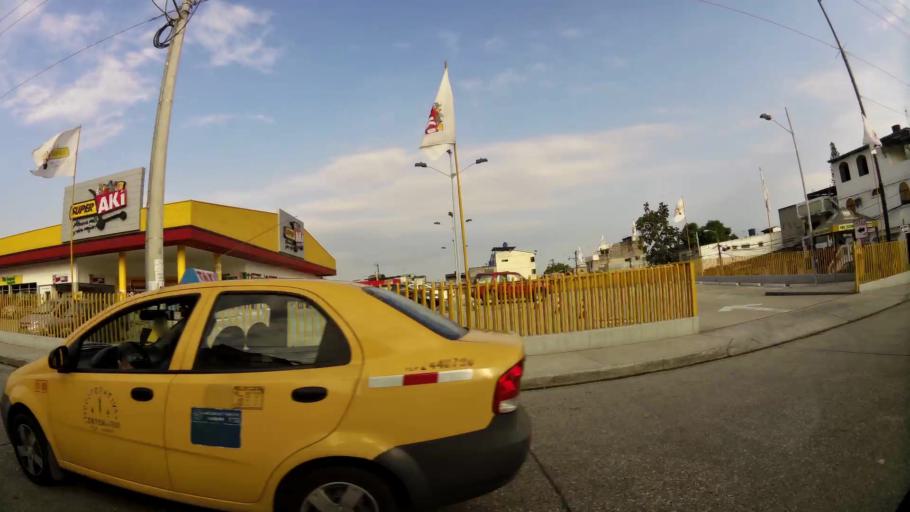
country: EC
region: Guayas
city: Eloy Alfaro
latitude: -2.1348
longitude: -79.8922
